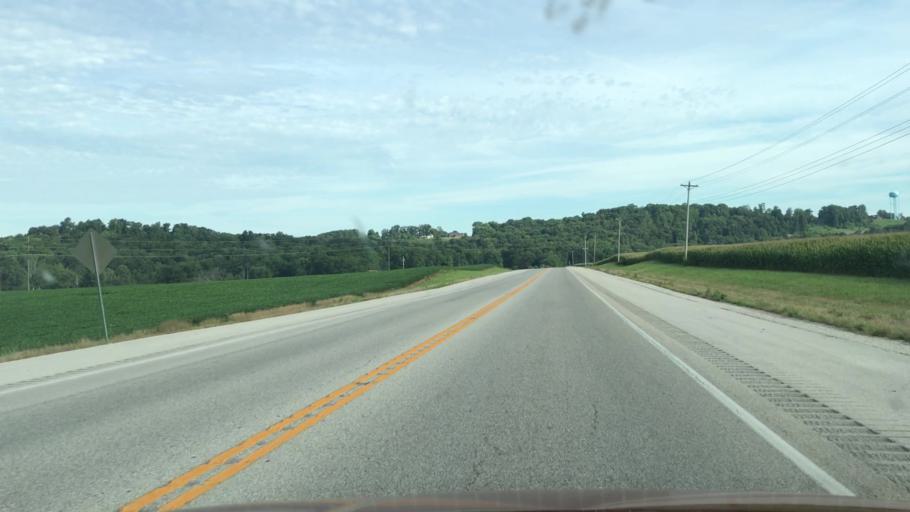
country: US
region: Kentucky
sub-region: Edmonson County
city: Brownsville
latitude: 37.0872
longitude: -86.2296
